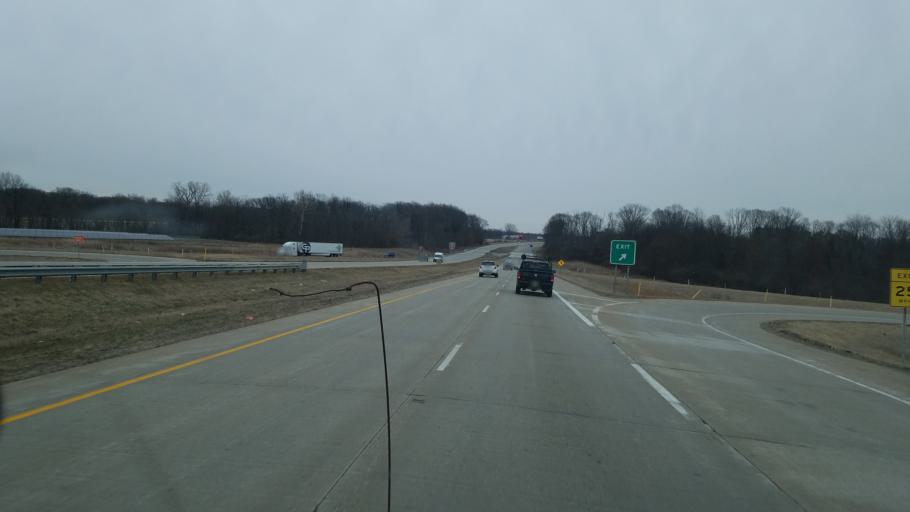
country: US
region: Indiana
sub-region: Marshall County
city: Plymouth
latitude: 41.3620
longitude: -86.3112
